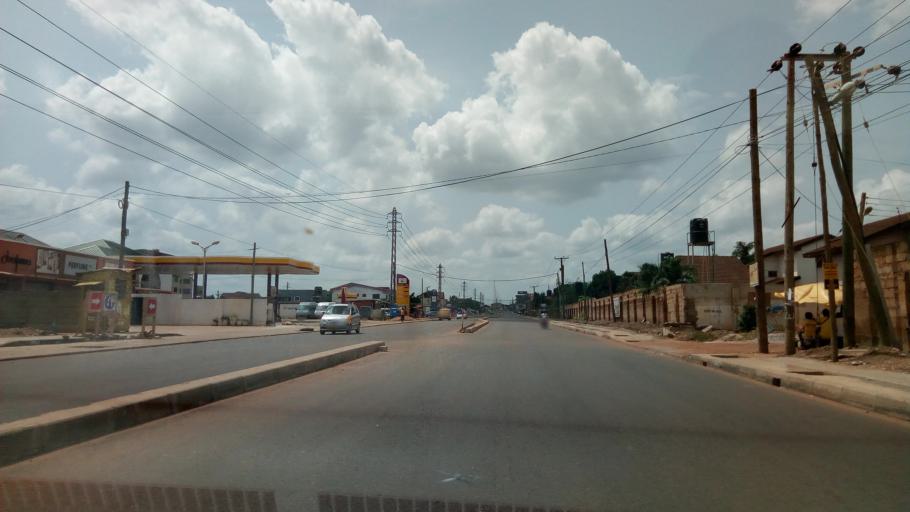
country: GH
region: Greater Accra
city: Medina Estates
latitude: 5.6695
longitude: -0.1286
